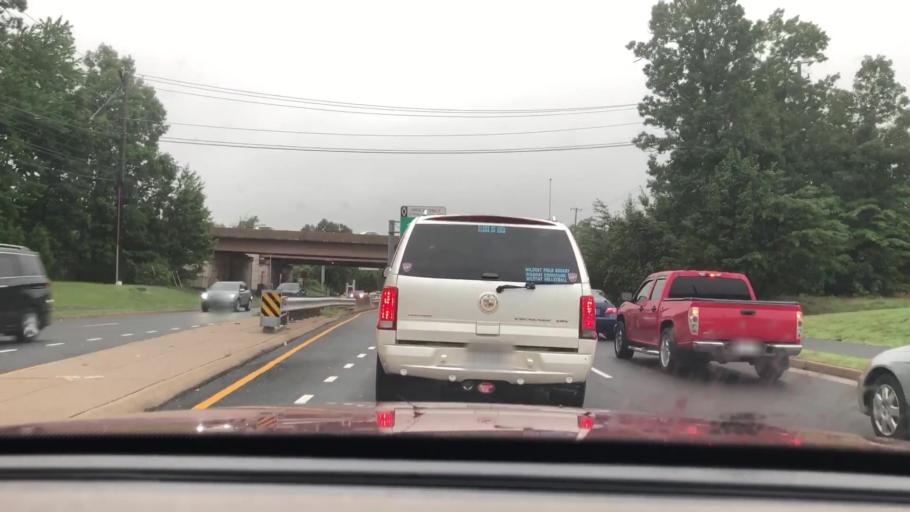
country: US
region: Virginia
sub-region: Fairfax County
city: Greenbriar
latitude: 38.8530
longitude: -77.4033
